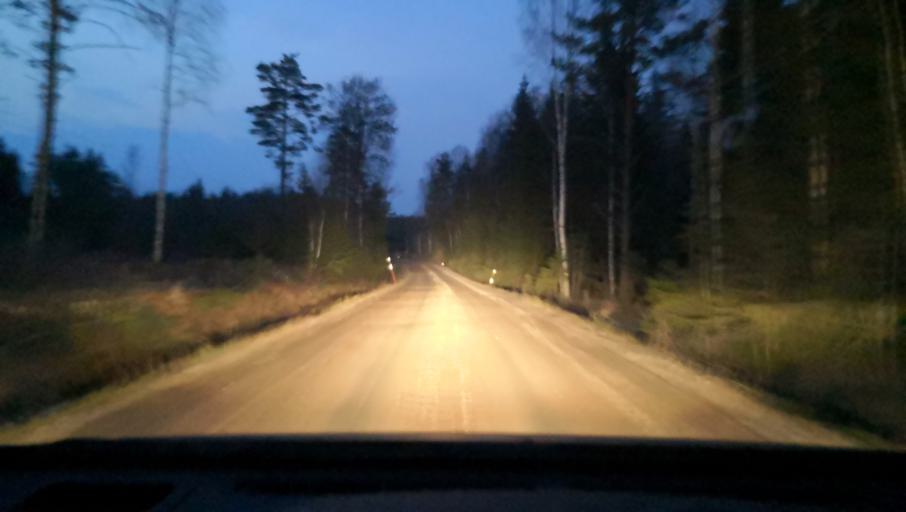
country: SE
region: OErebro
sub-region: Lindesbergs Kommun
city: Frovi
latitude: 59.6097
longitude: 15.4777
